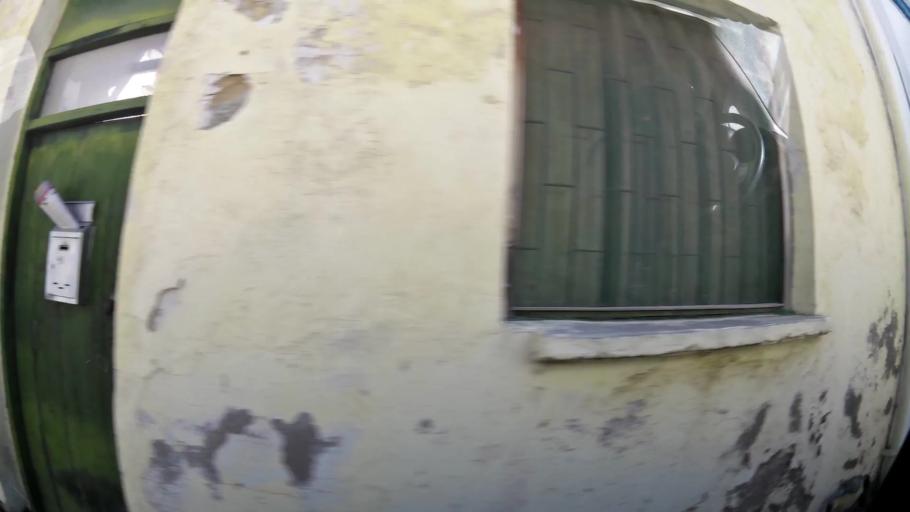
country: CY
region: Larnaka
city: Larnaca
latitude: 34.9068
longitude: 33.6371
